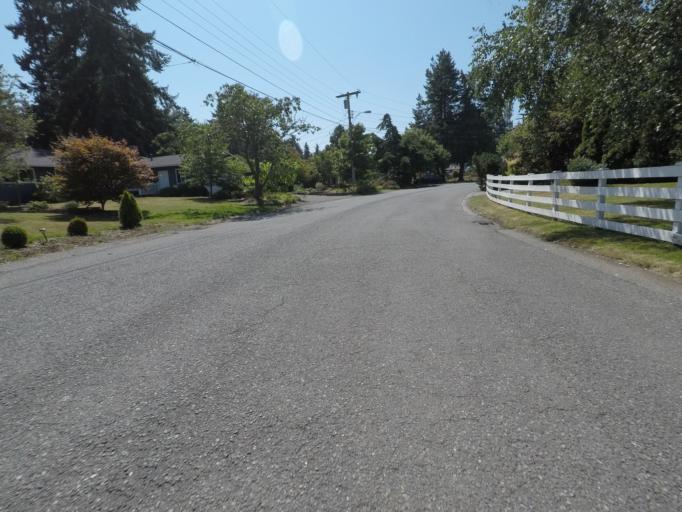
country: US
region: Washington
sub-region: King County
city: Inglewood-Finn Hill
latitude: 47.7319
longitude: -122.2405
